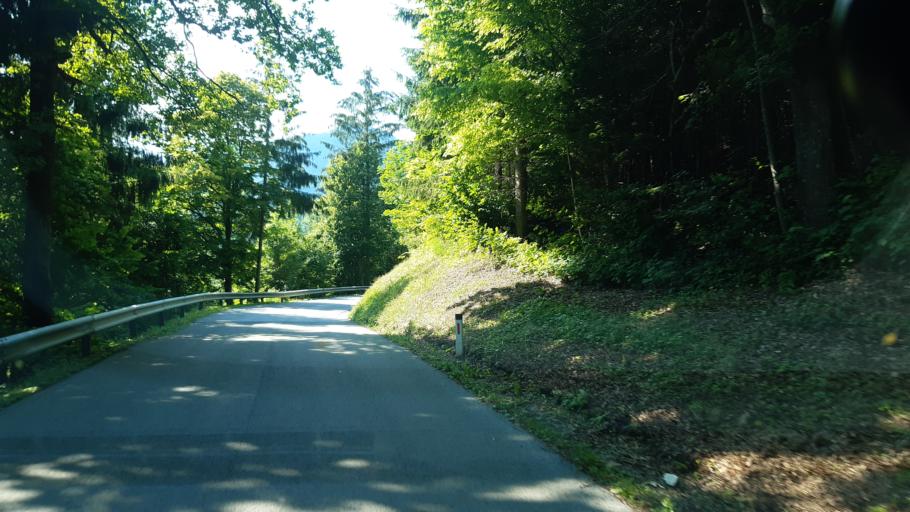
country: SI
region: Radovljica
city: Radovljica
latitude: 46.3763
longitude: 14.2157
